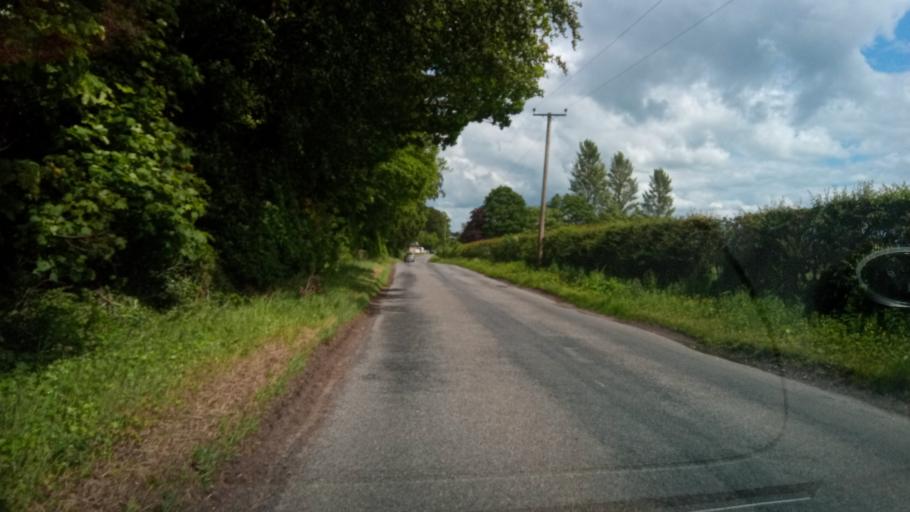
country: GB
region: Scotland
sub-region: The Scottish Borders
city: Kelso
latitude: 55.5823
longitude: -2.3886
